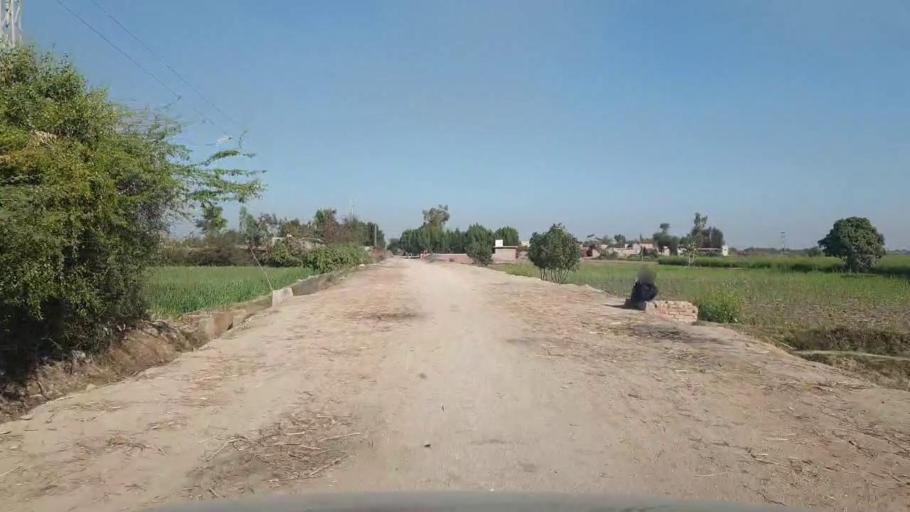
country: PK
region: Sindh
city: Mirwah Gorchani
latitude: 25.3085
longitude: 69.0923
